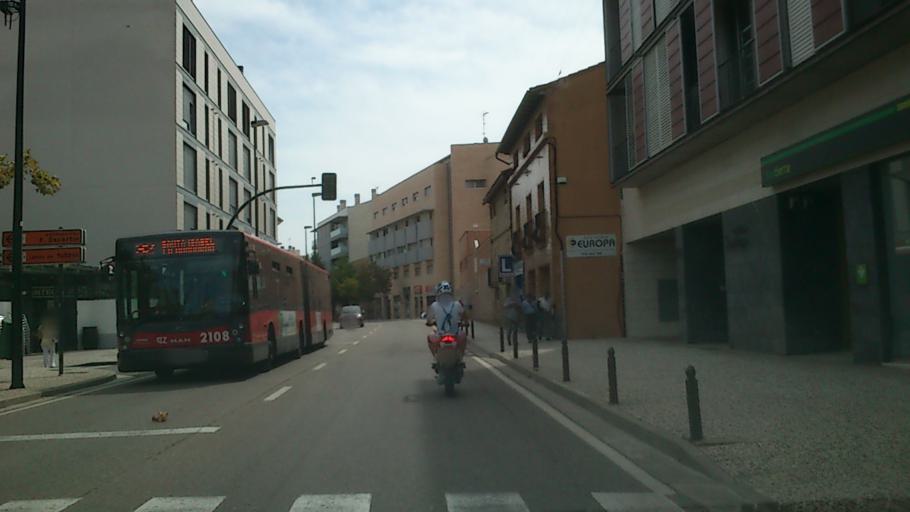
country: ES
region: Aragon
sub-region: Provincia de Zaragoza
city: Zaragoza
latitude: 41.6669
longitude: -0.8315
